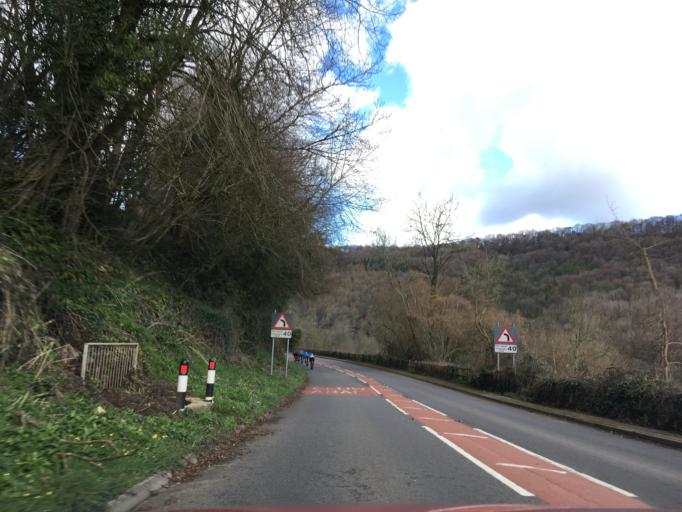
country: GB
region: Wales
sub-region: Monmouthshire
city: Tintern
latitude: 51.6899
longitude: -2.6718
